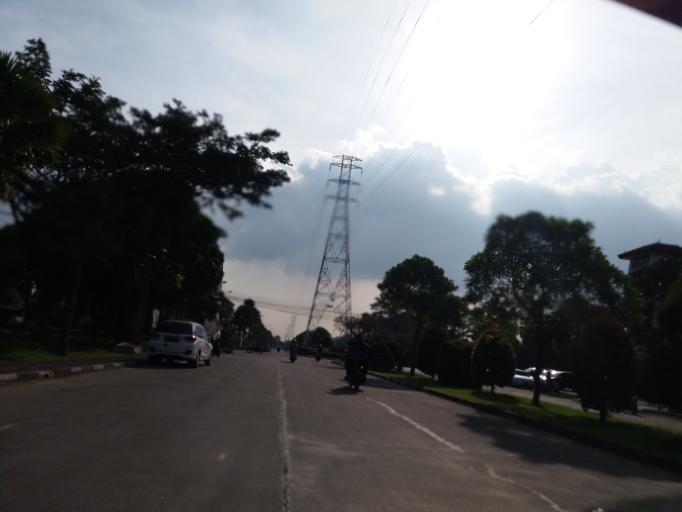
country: ID
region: West Java
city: Bandung
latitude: -6.9541
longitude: 107.6280
